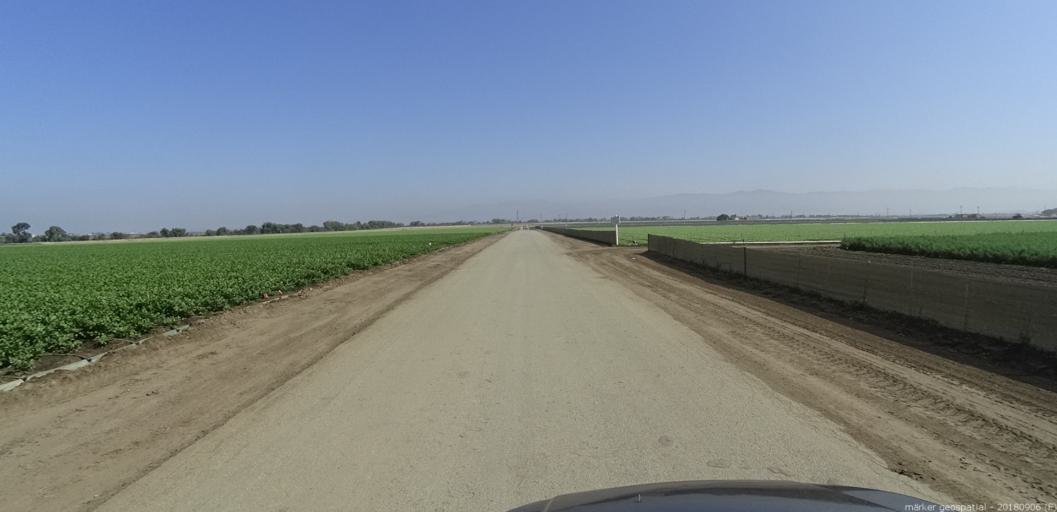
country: US
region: California
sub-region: Monterey County
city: Salinas
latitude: 36.5984
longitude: -121.6175
